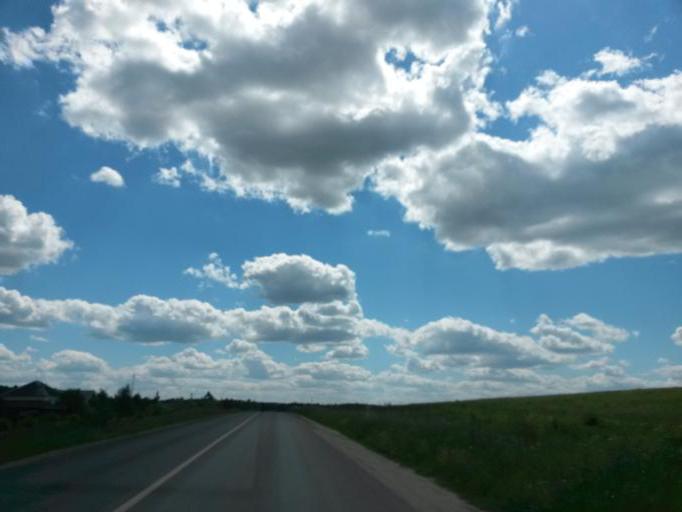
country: RU
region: Moskovskaya
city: Lyubuchany
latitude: 55.3023
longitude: 37.6376
